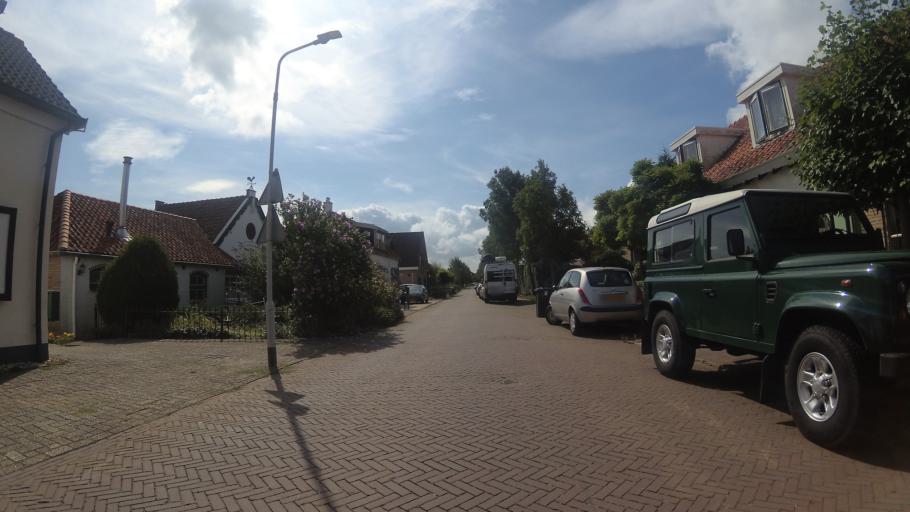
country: NL
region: Zeeland
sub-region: Schouwen-Duiveland
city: Haamstede
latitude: 51.6965
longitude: 3.7446
